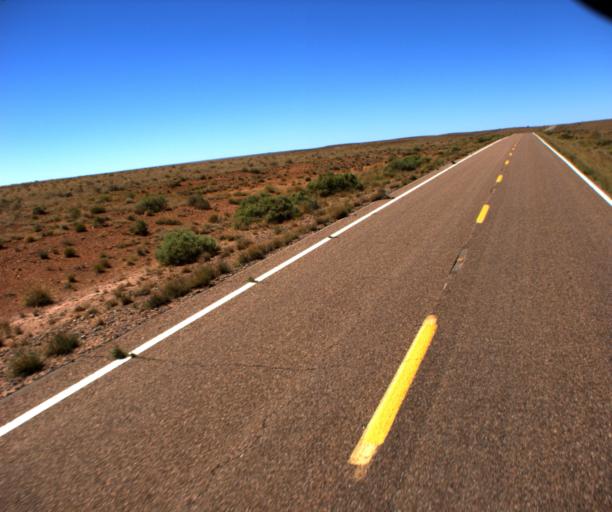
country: US
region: Arizona
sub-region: Navajo County
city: Winslow
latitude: 34.9126
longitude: -110.6386
